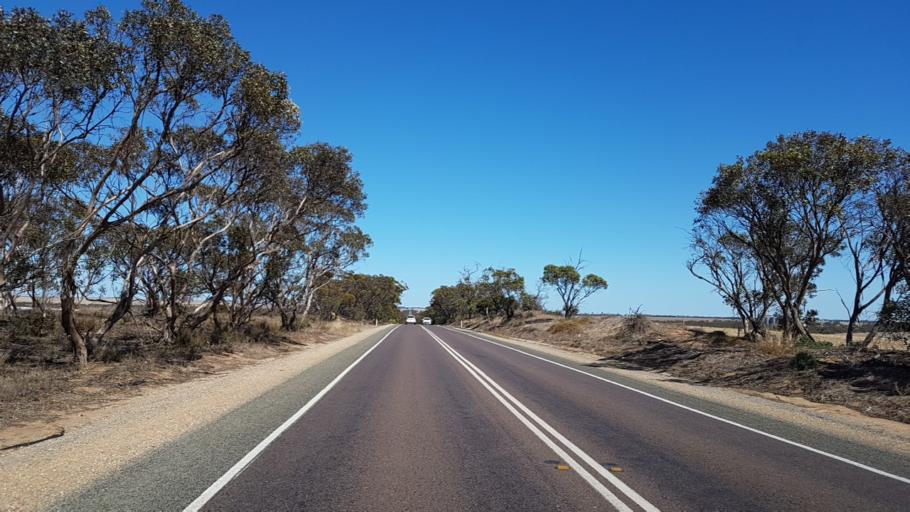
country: AU
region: South Australia
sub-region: Copper Coast
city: Kadina
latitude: -34.0534
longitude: 137.9974
